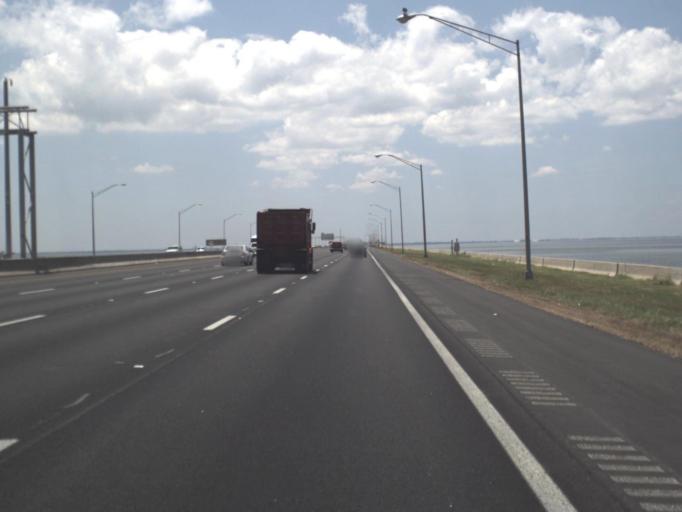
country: US
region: Florida
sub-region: Hillsborough County
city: Town 'n' Country
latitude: 27.9412
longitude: -82.5502
